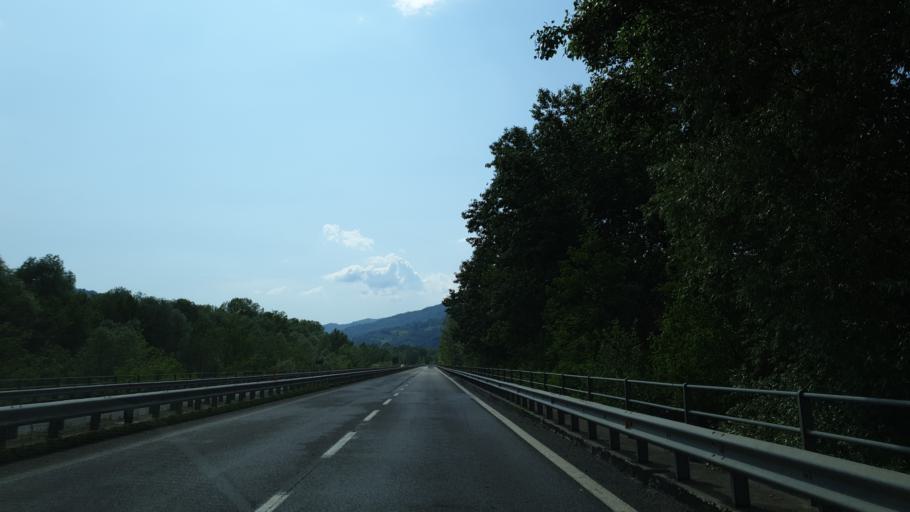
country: IT
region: Emilia-Romagna
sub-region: Forli-Cesena
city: Sarsina
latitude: 43.8887
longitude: 12.0628
